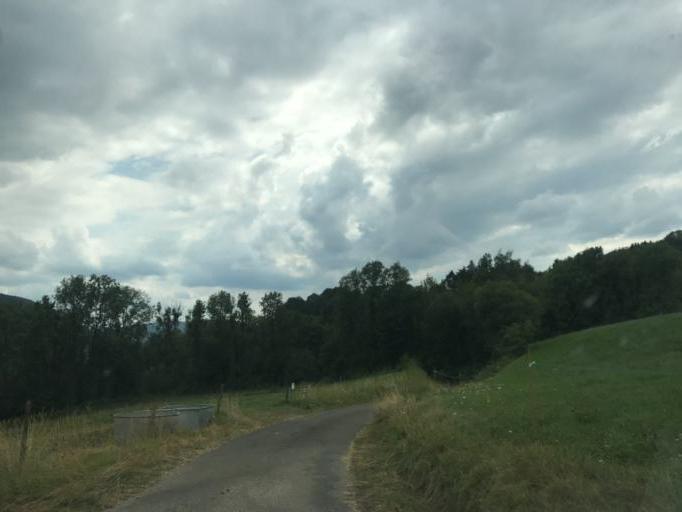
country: FR
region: Franche-Comte
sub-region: Departement du Jura
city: Longchaumois
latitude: 46.4672
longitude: 5.8919
